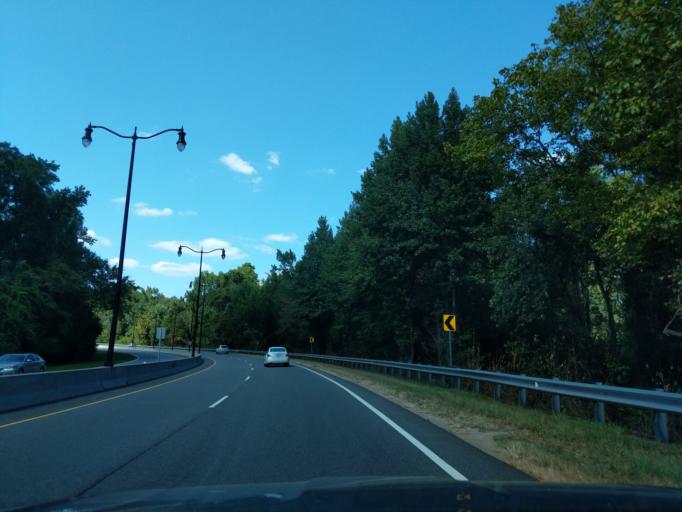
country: US
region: South Carolina
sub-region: Aiken County
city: North Augusta
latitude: 33.5160
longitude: -82.0041
